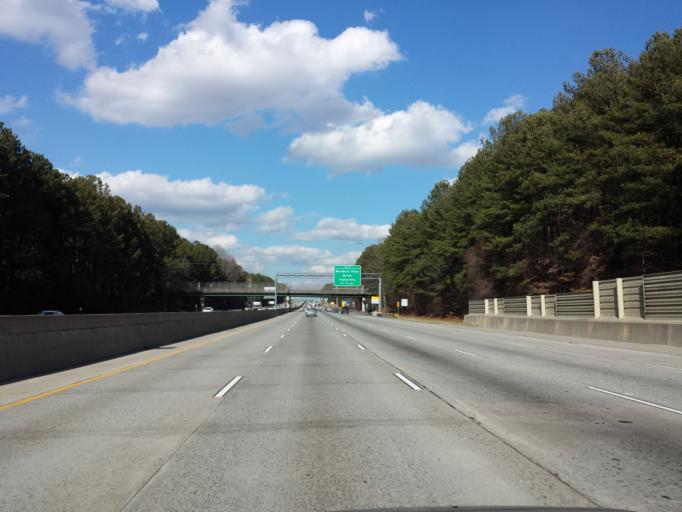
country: US
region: Georgia
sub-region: Fulton County
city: Alpharetta
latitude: 34.0729
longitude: -84.2696
